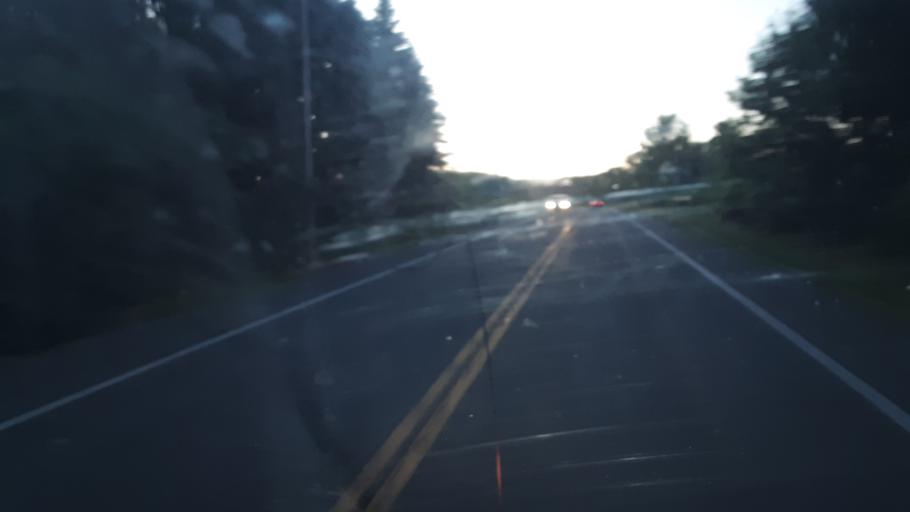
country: US
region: New York
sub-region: Montgomery County
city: Hagaman
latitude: 42.9700
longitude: -74.0814
